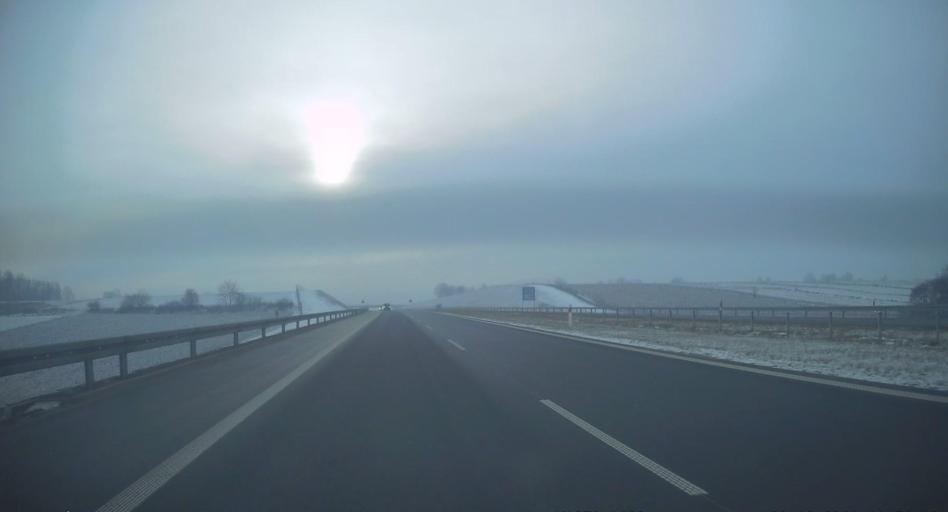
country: PL
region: Lesser Poland Voivodeship
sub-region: Powiat krakowski
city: Slomniki
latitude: 50.2772
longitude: 20.0214
